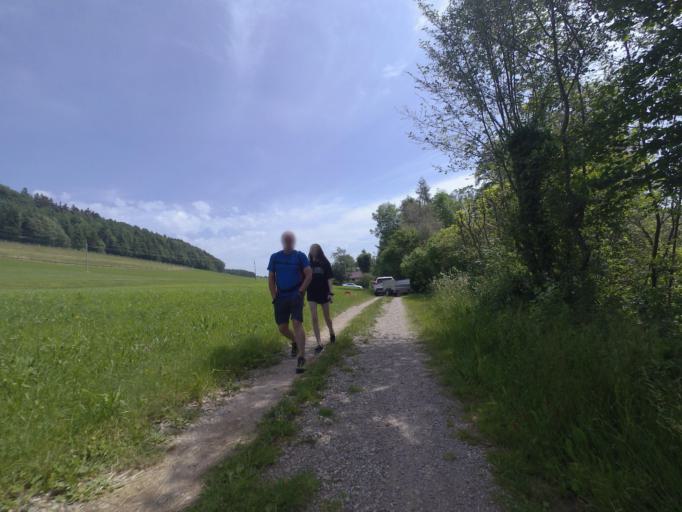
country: AT
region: Salzburg
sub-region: Politischer Bezirk Salzburg-Umgebung
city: Schleedorf
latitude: 47.9946
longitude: 13.1449
